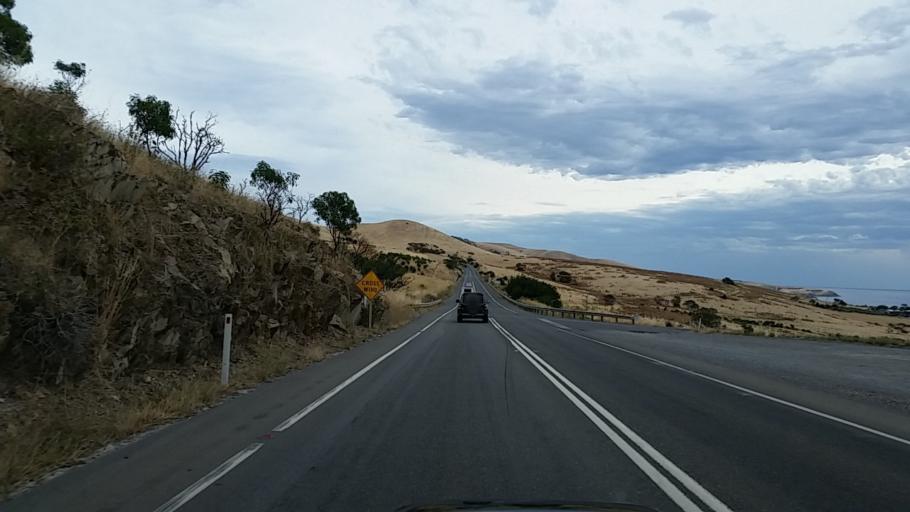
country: AU
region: South Australia
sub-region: Onkaparinga
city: Aldinga
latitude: -35.3400
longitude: 138.4626
